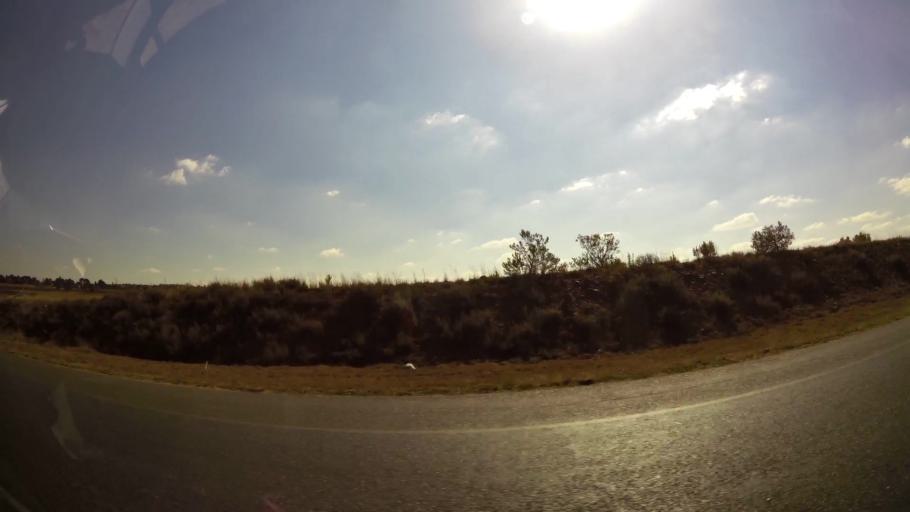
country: ZA
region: Gauteng
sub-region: West Rand District Municipality
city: Randfontein
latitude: -26.1769
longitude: 27.7681
